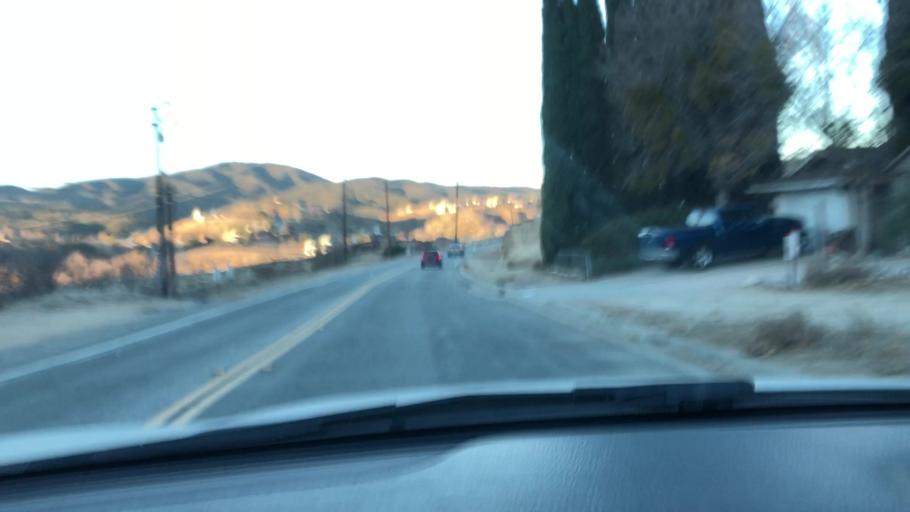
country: US
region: California
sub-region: Los Angeles County
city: Green Valley
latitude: 34.6599
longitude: -118.3687
